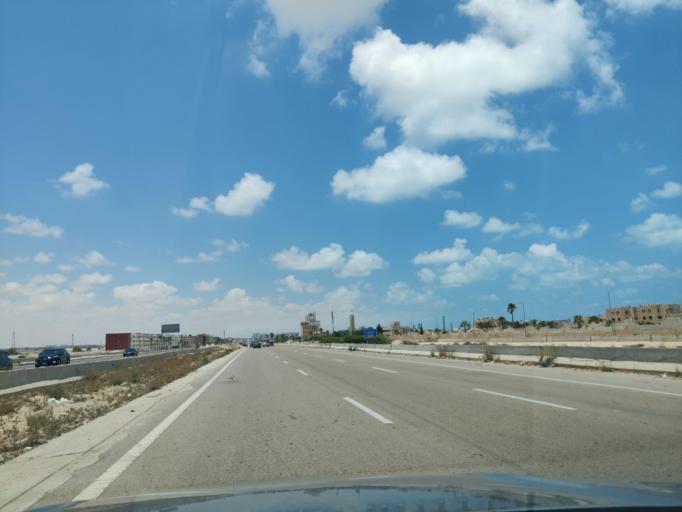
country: EG
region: Muhafazat Matruh
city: Al `Alamayn
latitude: 30.8156
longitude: 29.0369
